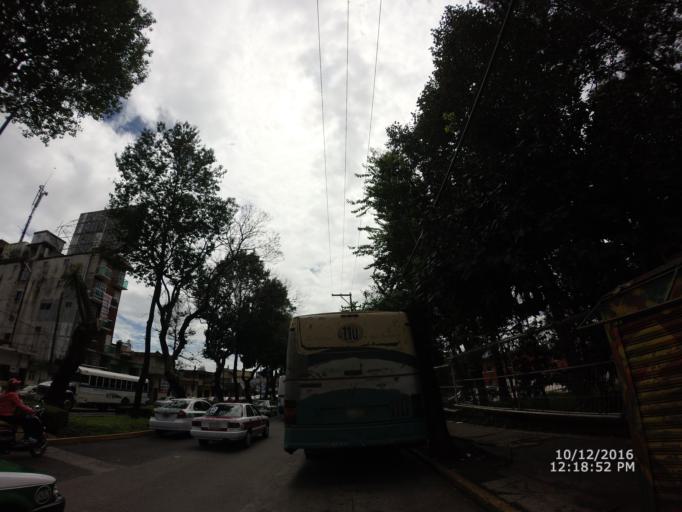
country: MX
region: Veracruz
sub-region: Xalapa
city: Xalapa de Enriquez
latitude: 19.5425
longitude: -96.9271
